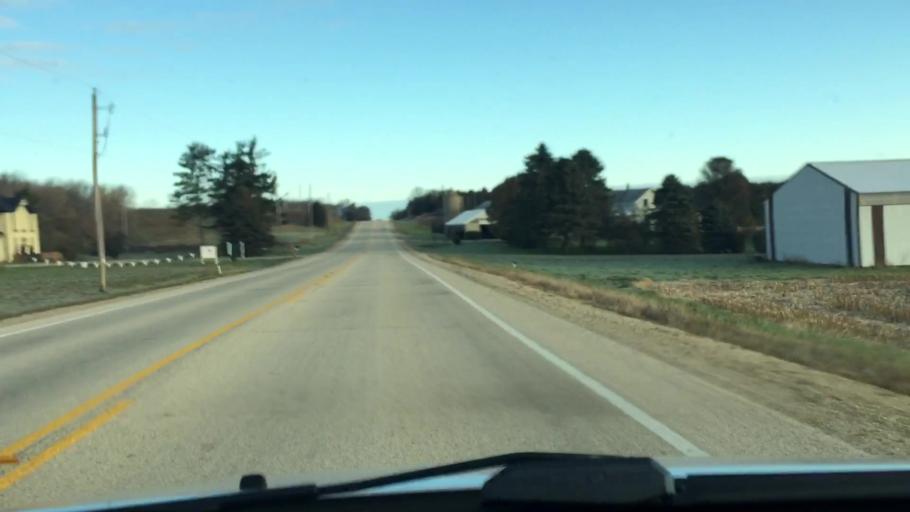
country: US
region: Wisconsin
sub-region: Washington County
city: Hartford
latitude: 43.2711
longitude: -88.4636
